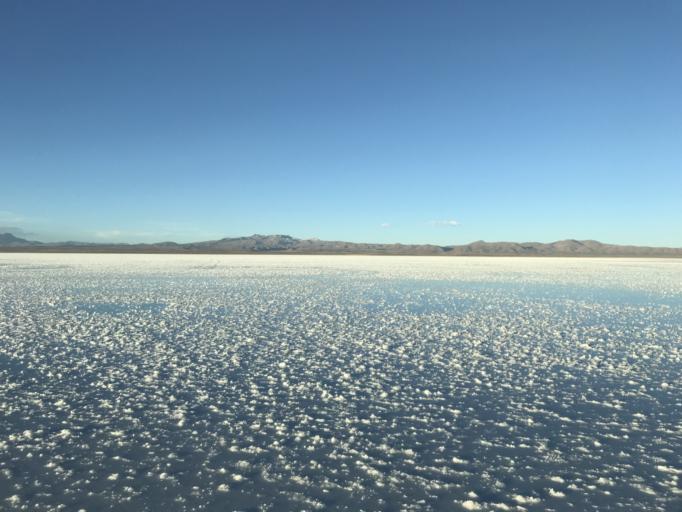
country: BO
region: Potosi
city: Colchani
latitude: -20.3851
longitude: -66.9851
